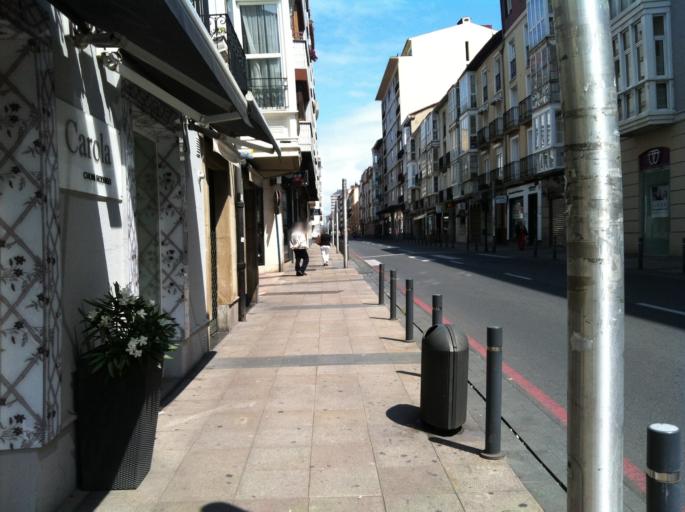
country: ES
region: Basque Country
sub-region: Provincia de Alava
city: Gasteiz / Vitoria
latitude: 42.8431
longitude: -2.6724
